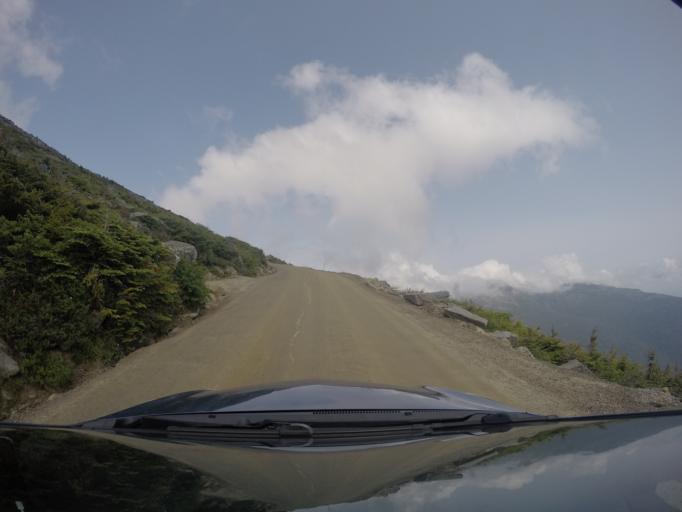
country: US
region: New Hampshire
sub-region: Coos County
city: Gorham
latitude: 44.2842
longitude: -71.2797
